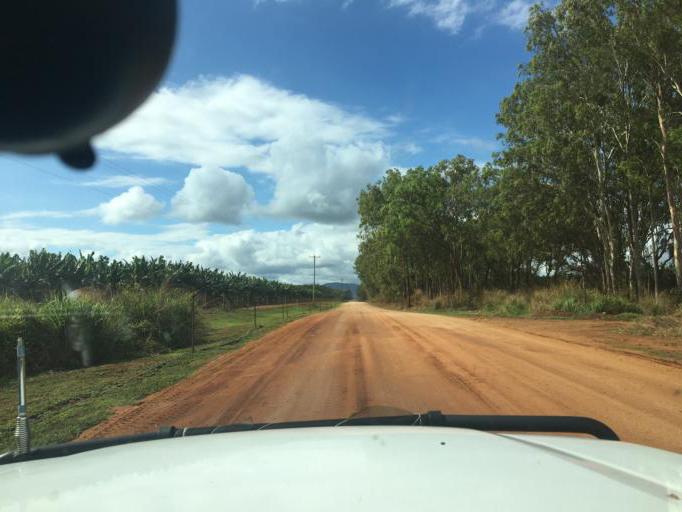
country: AU
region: Queensland
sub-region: Tablelands
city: Mareeba
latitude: -17.0944
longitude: 145.4122
